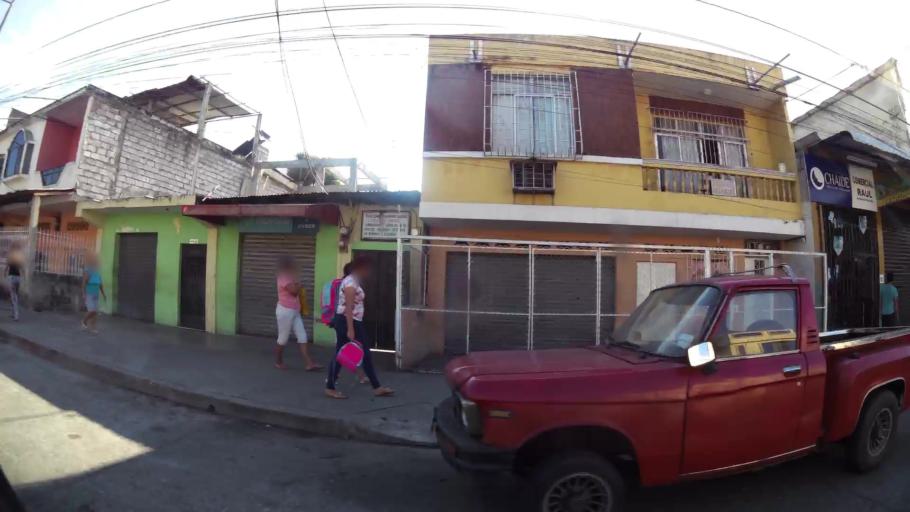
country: EC
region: Guayas
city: Guayaquil
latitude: -2.2258
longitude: -79.9293
